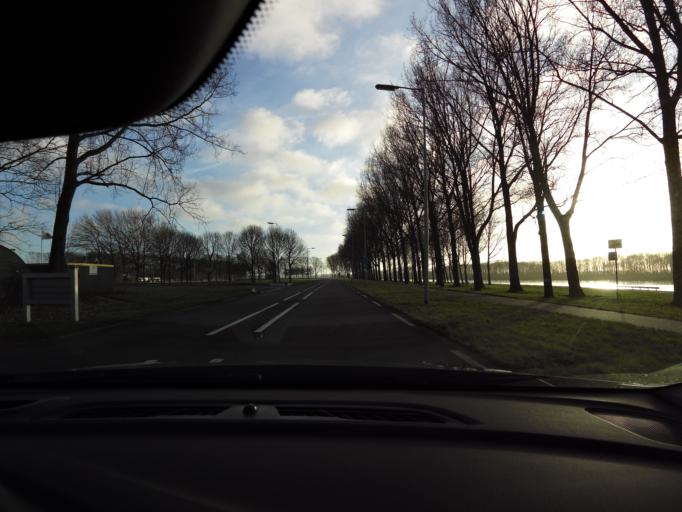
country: NL
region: South Holland
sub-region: Gemeente Maassluis
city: Maassluis
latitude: 51.8948
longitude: 4.2266
